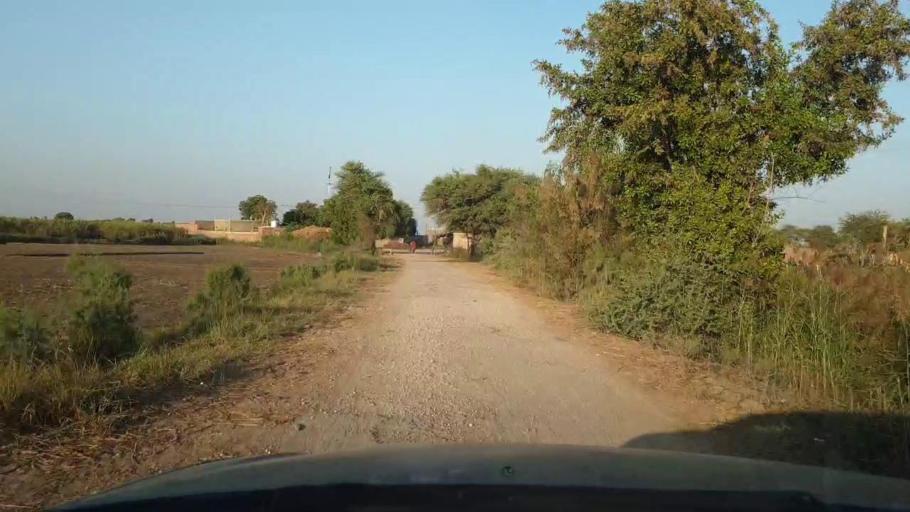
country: PK
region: Sindh
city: Matli
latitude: 25.0350
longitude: 68.6276
